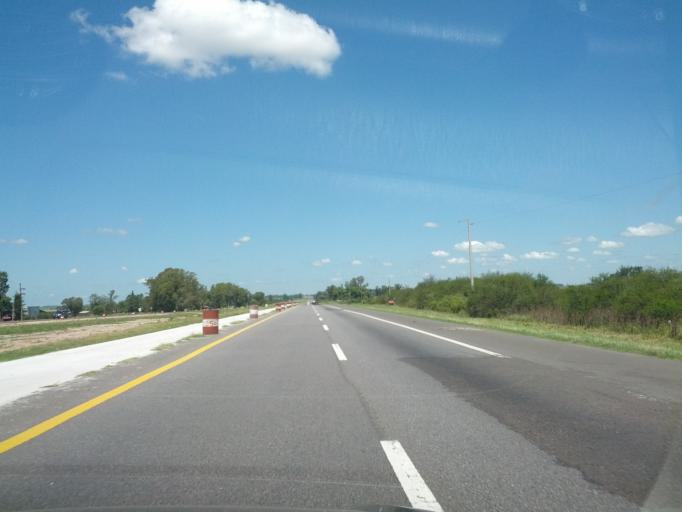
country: AR
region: Entre Rios
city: Gualeguaychu
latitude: -33.1181
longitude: -58.6514
